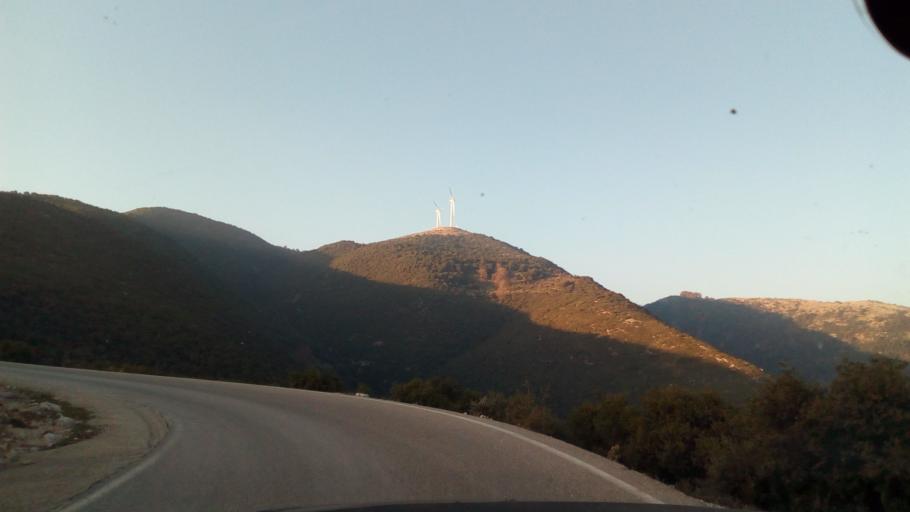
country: GR
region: West Greece
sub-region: Nomos Aitolias kai Akarnanias
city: Nafpaktos
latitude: 38.4323
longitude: 21.8579
